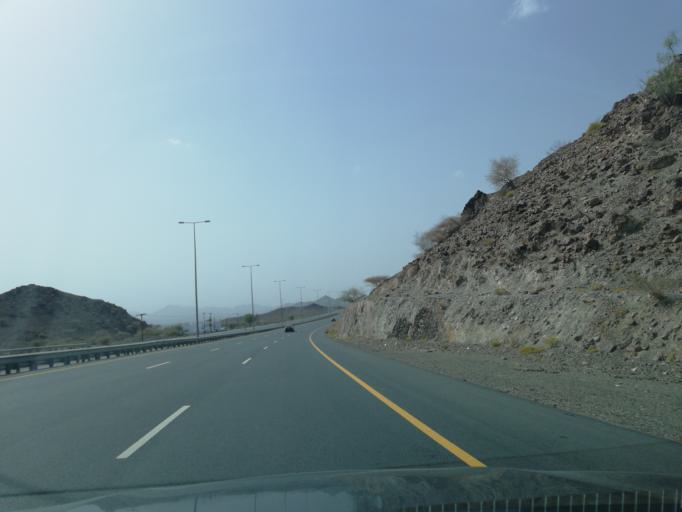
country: OM
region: Ash Sharqiyah
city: Ibra'
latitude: 22.8954
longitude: 58.2755
